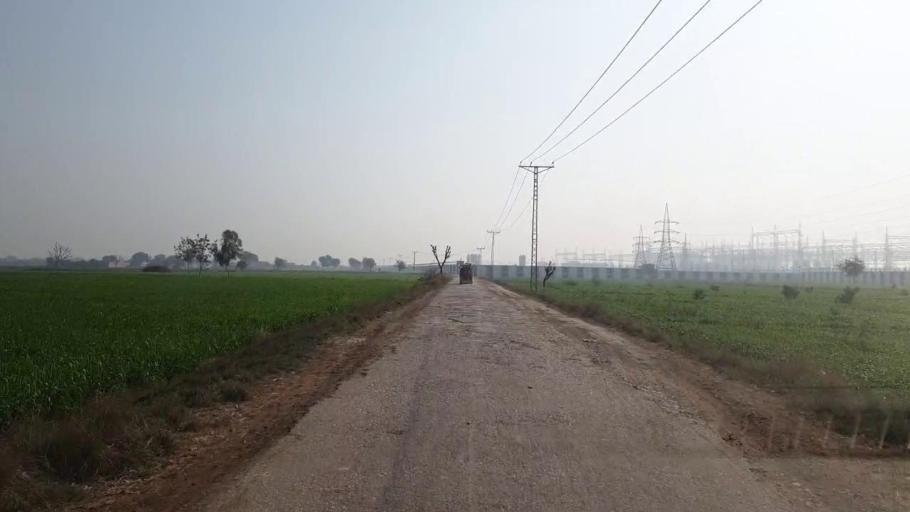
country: PK
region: Sindh
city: Bhit Shah
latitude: 25.7184
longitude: 68.5126
